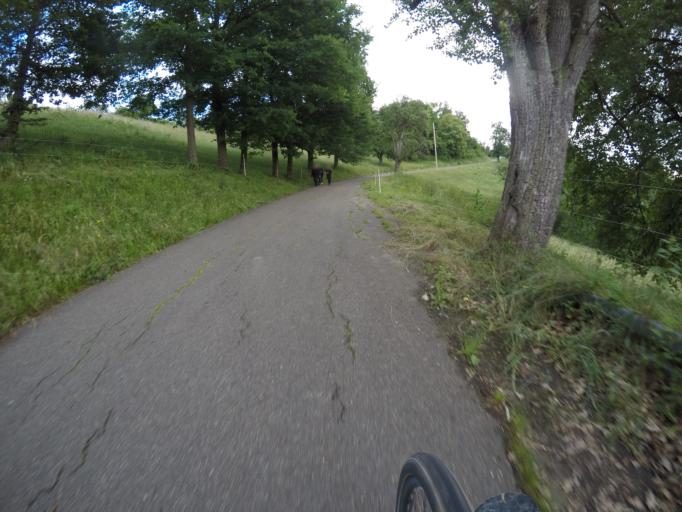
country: DE
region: Baden-Wuerttemberg
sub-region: Regierungsbezirk Stuttgart
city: Kohlberg
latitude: 48.5733
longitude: 9.3274
